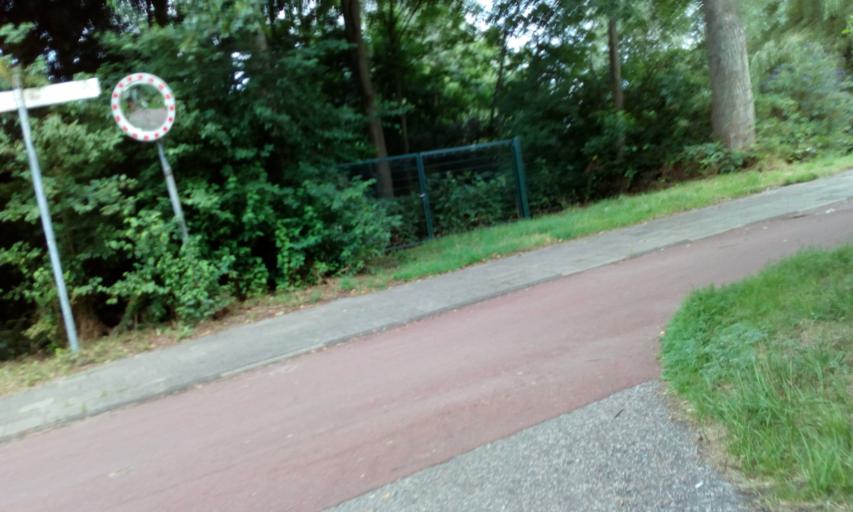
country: NL
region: South Holland
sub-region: Gemeente Zoetermeer
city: Zoetermeer
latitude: 52.0508
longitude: 4.4687
